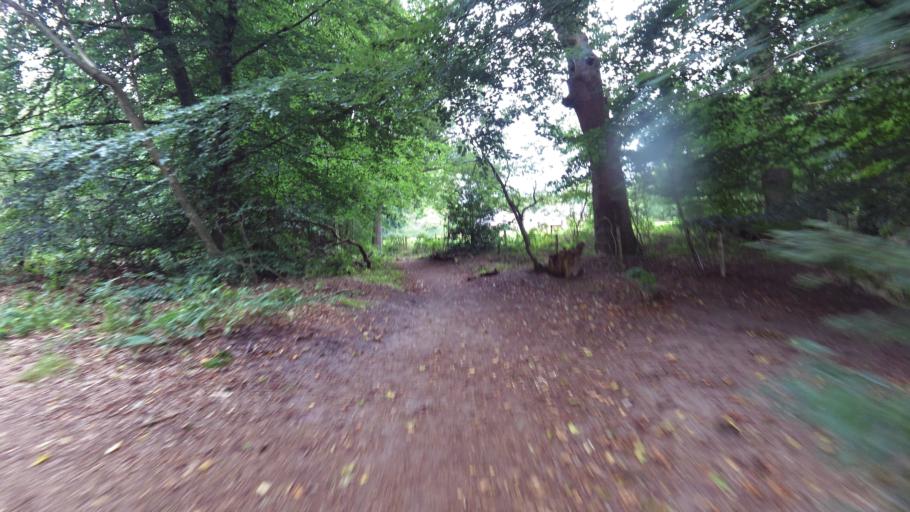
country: NL
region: Gelderland
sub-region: Gemeente Renkum
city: Renkum
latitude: 51.9886
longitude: 5.7282
